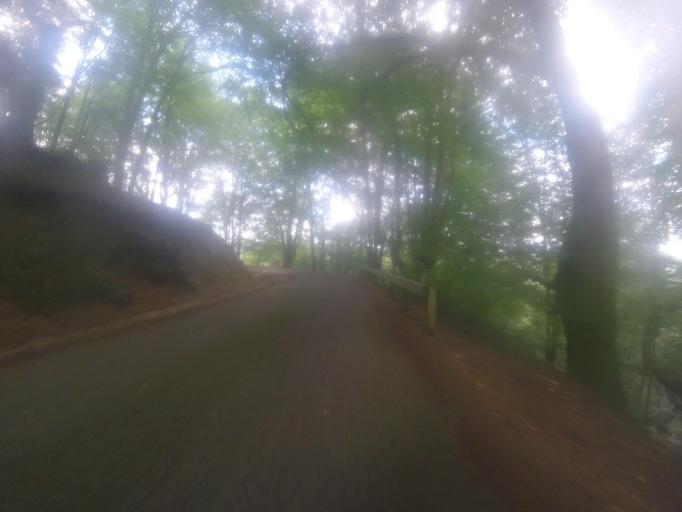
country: ES
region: Navarre
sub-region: Provincia de Navarra
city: Goizueta
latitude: 43.2280
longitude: -1.8040
